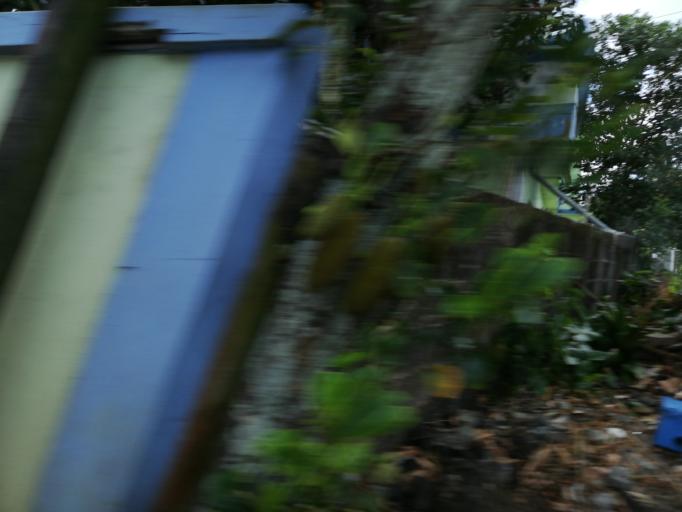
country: MU
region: Riviere du Rempart
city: Esperance Trebuchet
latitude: -20.0772
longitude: 57.6517
